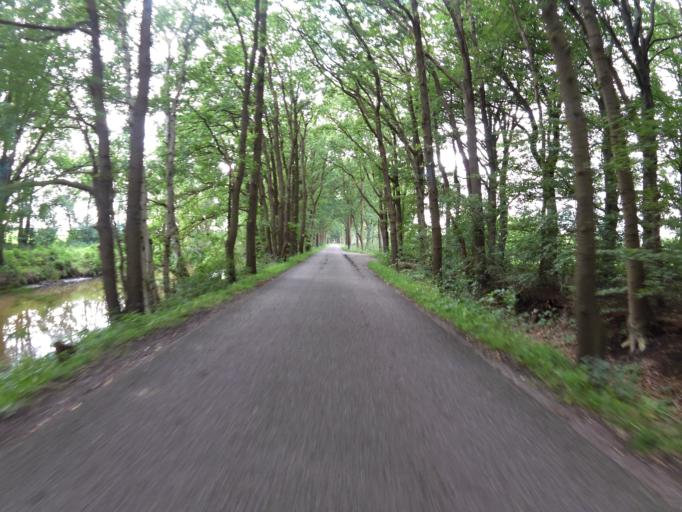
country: NL
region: North Holland
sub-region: Gemeente Wijdemeren
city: Nieuw-Loosdrecht
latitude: 52.1795
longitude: 5.1563
